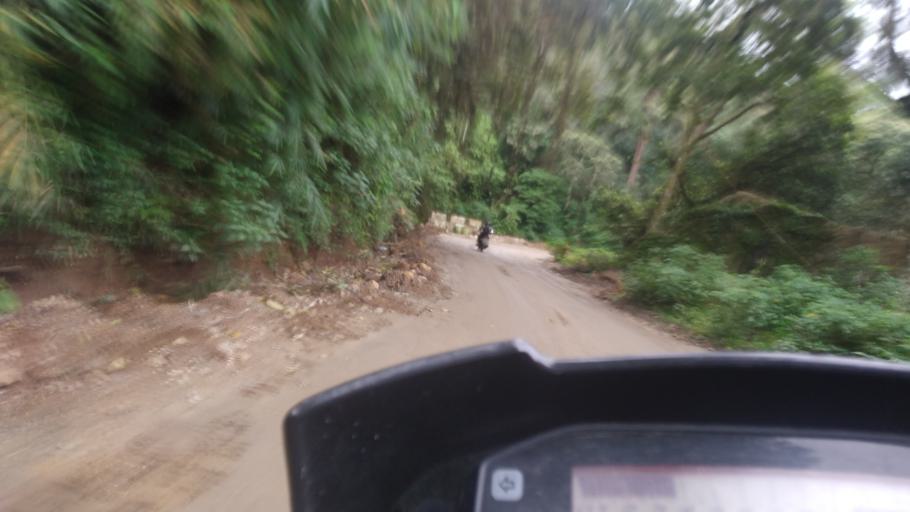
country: IN
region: Kerala
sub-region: Idukki
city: Munnar
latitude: 10.0359
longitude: 77.1401
